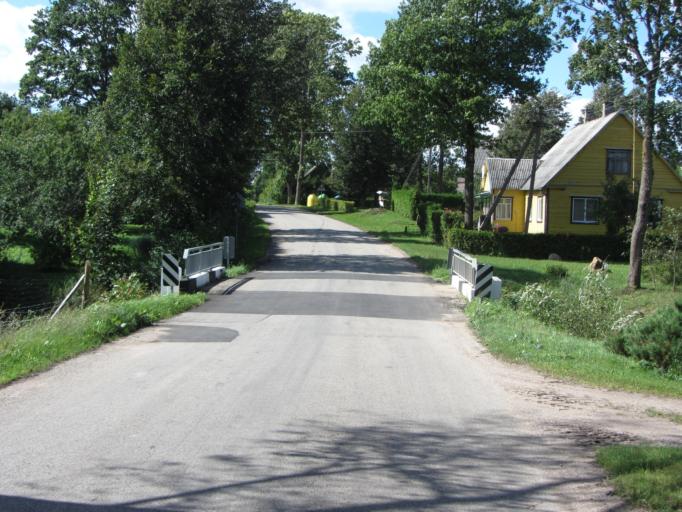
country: LV
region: Nereta
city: Nereta
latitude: 56.0996
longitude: 25.4223
